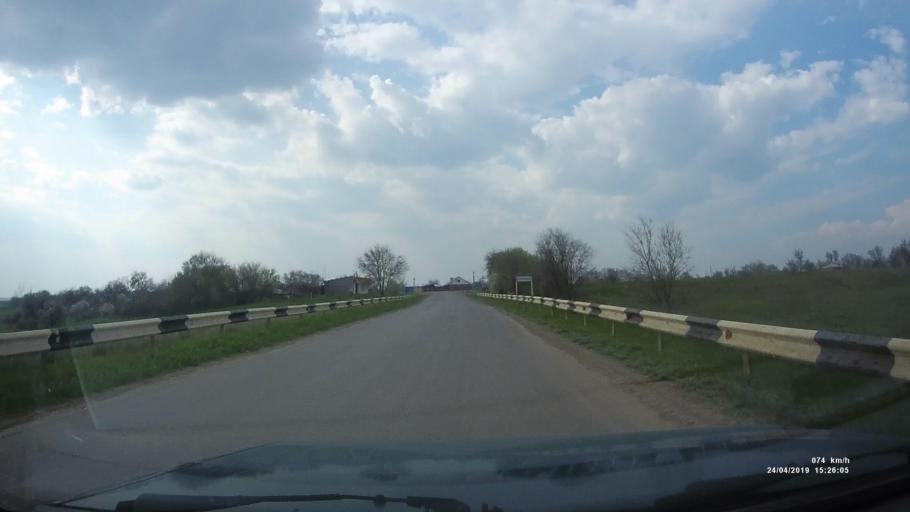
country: RU
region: Rostov
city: Remontnoye
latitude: 46.5563
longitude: 43.0374
